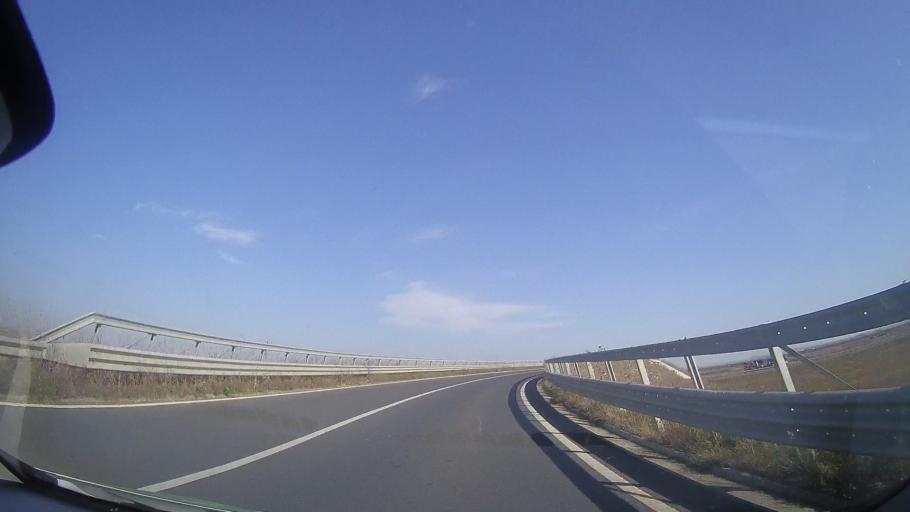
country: RO
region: Timis
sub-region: Comuna Belint
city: Belint
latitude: 45.7790
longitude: 21.7315
